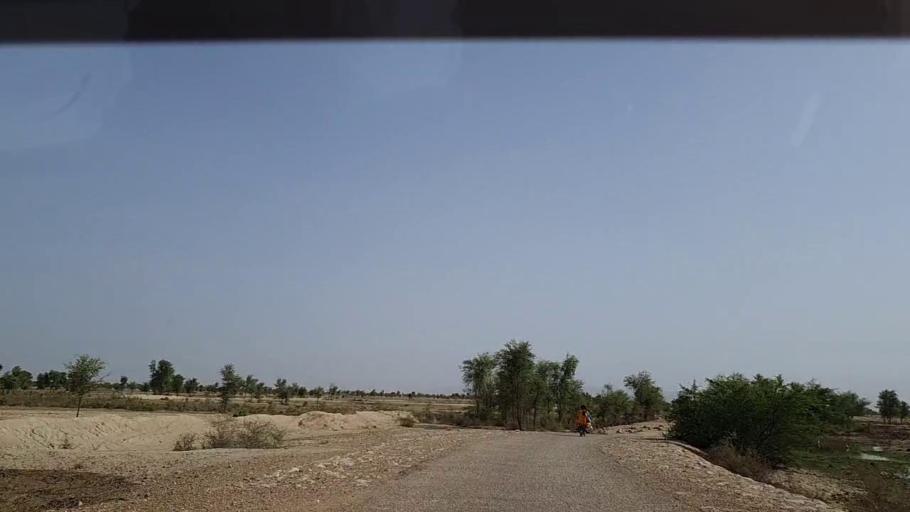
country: PK
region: Sindh
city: Johi
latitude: 26.6240
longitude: 67.5004
